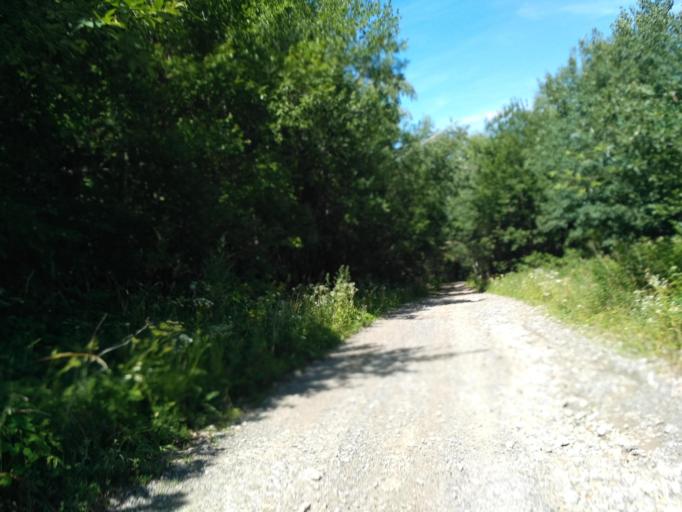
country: PL
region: Subcarpathian Voivodeship
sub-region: Powiat sanocki
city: Bukowsko
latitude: 49.4897
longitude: 22.0904
